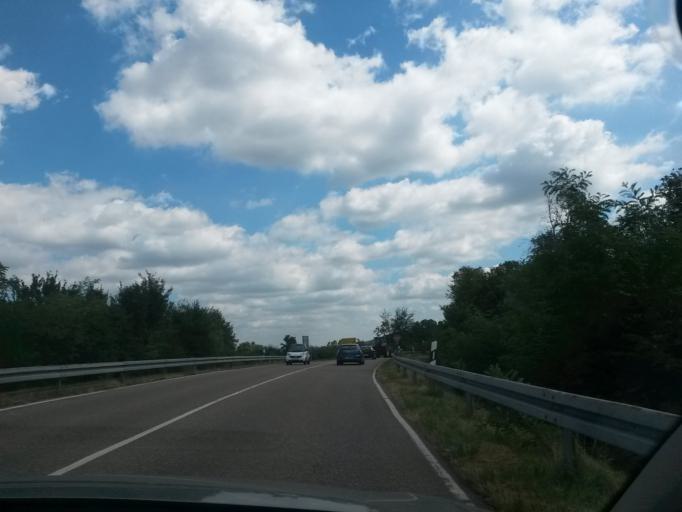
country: DE
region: Baden-Wuerttemberg
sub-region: Karlsruhe Region
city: Ettlingen
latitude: 48.9309
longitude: 8.3766
